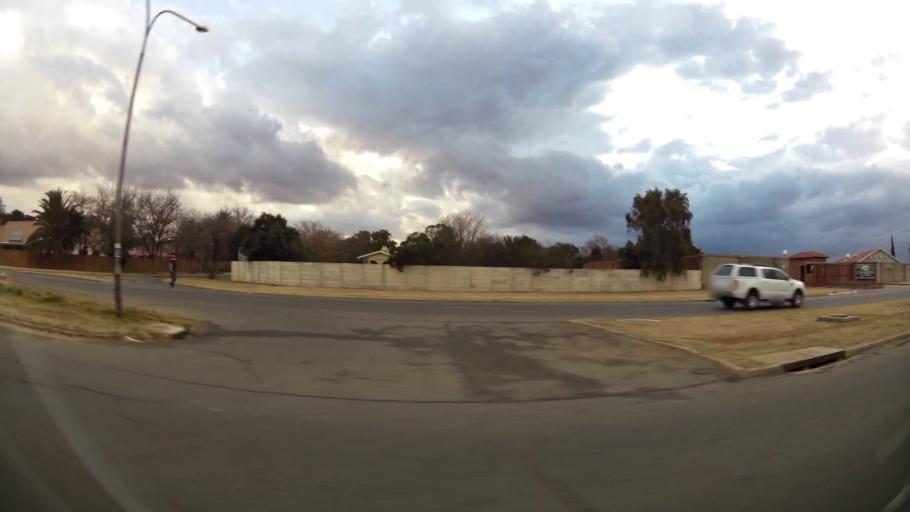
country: ZA
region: Orange Free State
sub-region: Lejweleputswa District Municipality
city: Welkom
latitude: -27.9579
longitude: 26.7368
